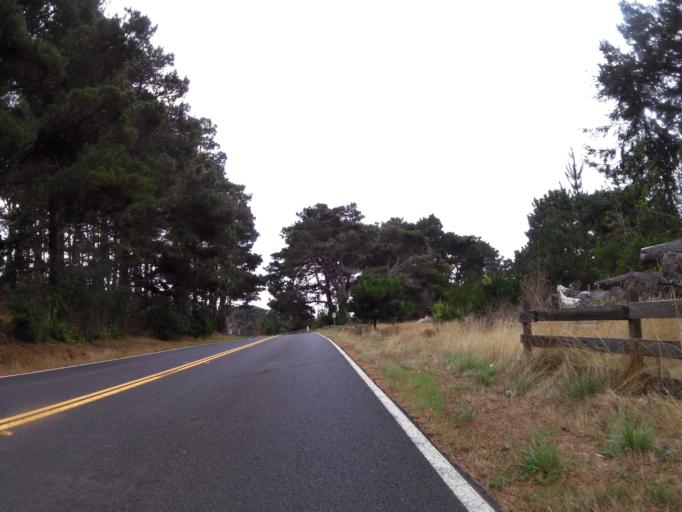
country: US
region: California
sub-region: Sonoma County
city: Sea Ranch
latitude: 38.5507
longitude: -123.3018
